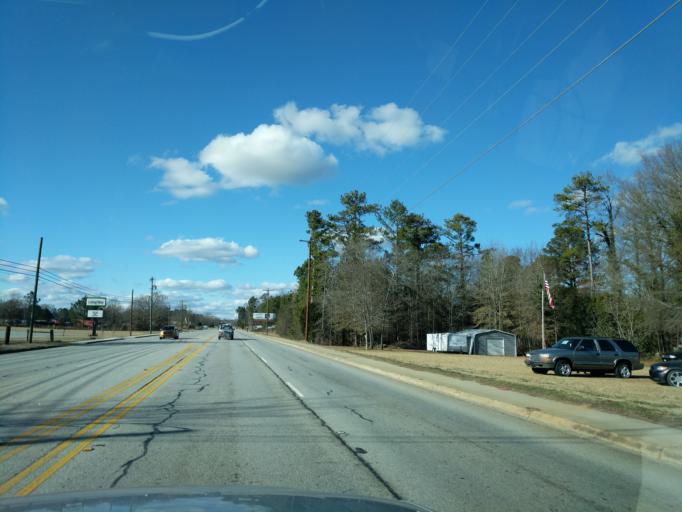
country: US
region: South Carolina
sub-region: Greenwood County
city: Greenwood
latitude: 34.1223
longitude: -82.1173
